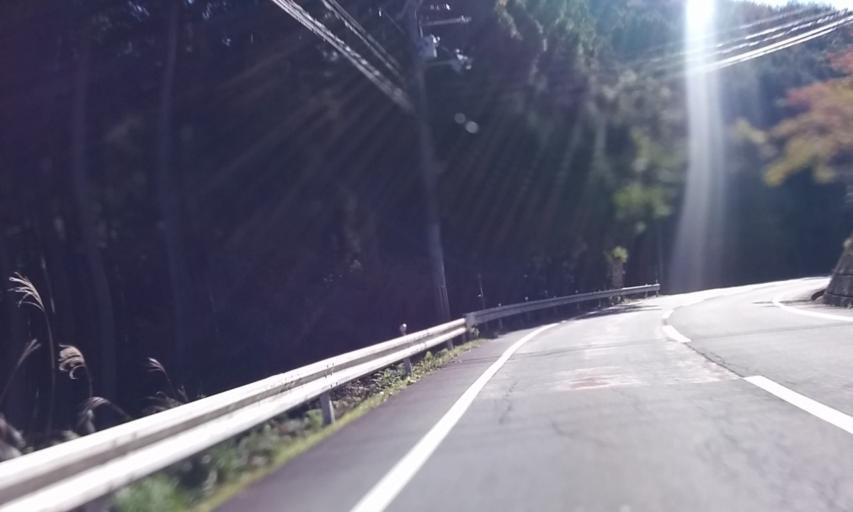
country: JP
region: Kyoto
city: Kameoka
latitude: 35.1982
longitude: 135.6203
